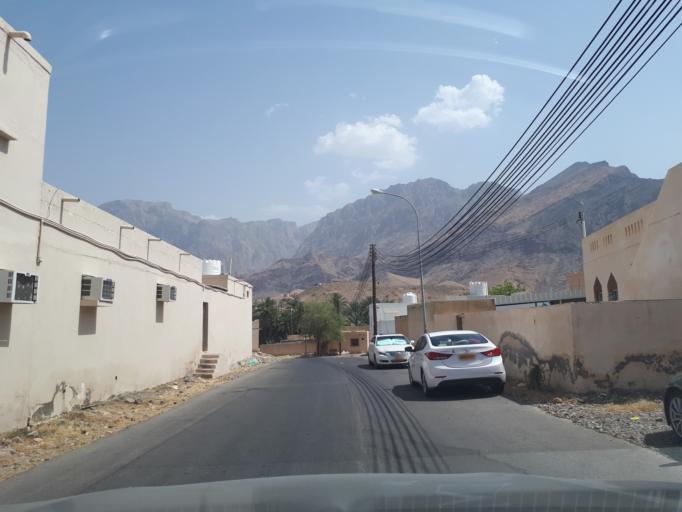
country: OM
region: Ash Sharqiyah
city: Ibra'
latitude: 23.0919
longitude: 58.8623
